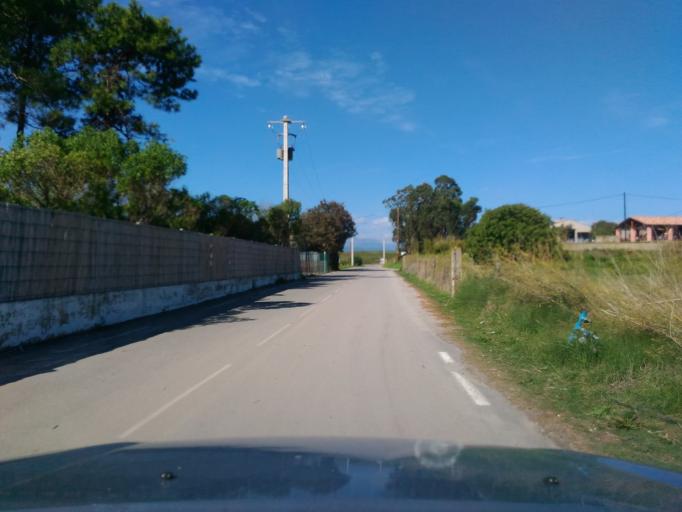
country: FR
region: Corsica
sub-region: Departement de la Haute-Corse
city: Aleria
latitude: 42.1114
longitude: 9.5509
